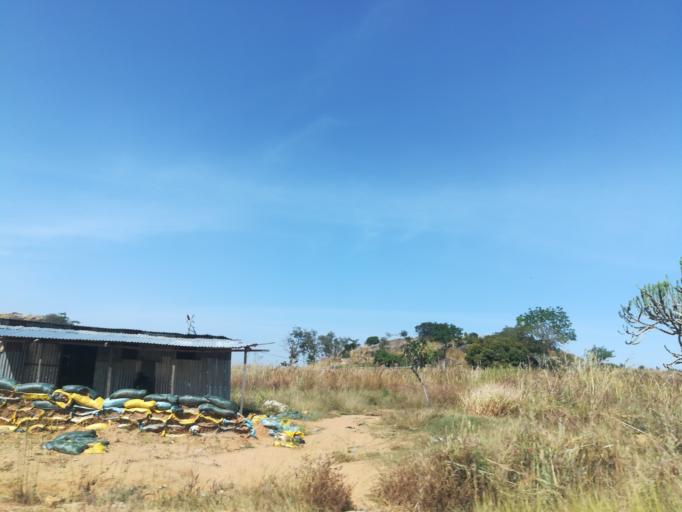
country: NG
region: Plateau
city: Bukuru
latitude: 9.7568
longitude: 8.9077
